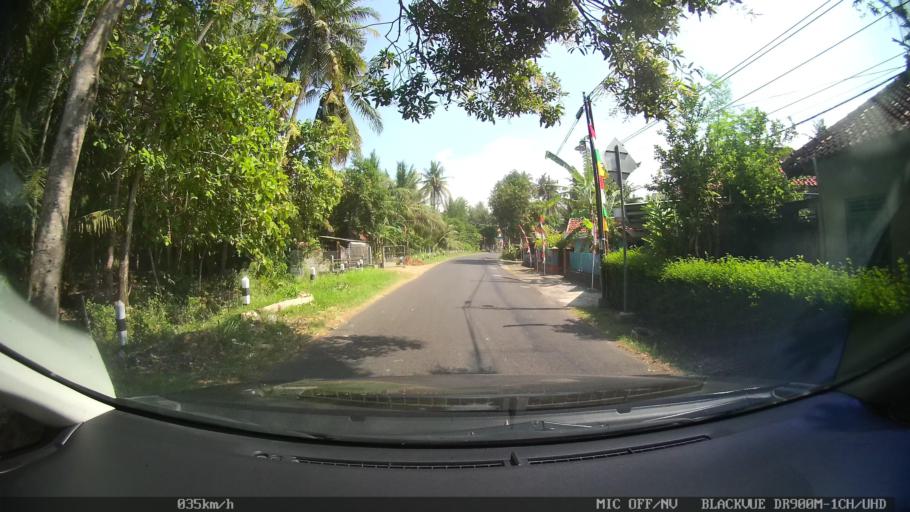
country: ID
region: Daerah Istimewa Yogyakarta
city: Srandakan
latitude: -7.9103
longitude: 110.1531
